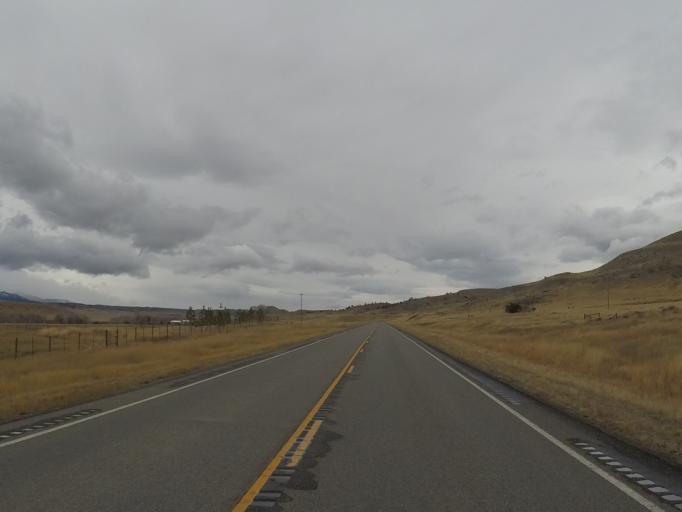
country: US
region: Montana
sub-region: Sweet Grass County
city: Big Timber
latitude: 45.9182
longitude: -109.9787
